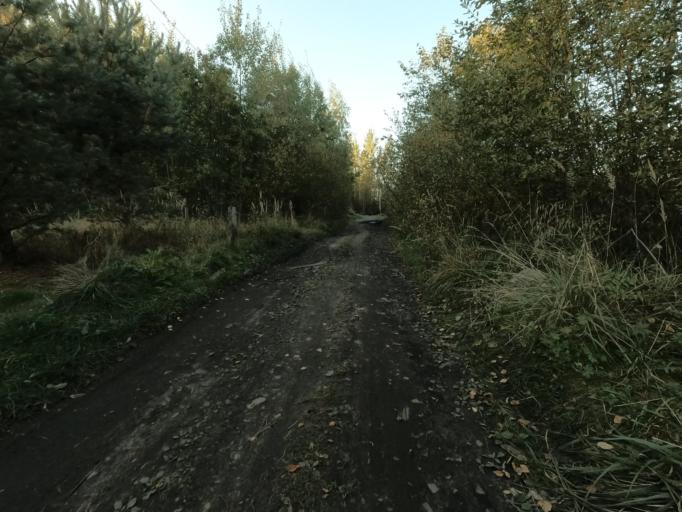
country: RU
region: Leningrad
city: Nikol'skoye
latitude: 59.7119
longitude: 30.7972
